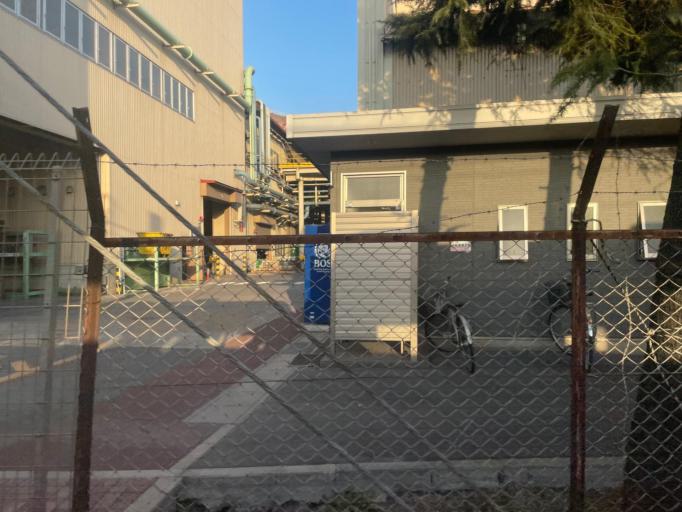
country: JP
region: Gunma
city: Shibukawa
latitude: 36.4834
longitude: 139.0068
